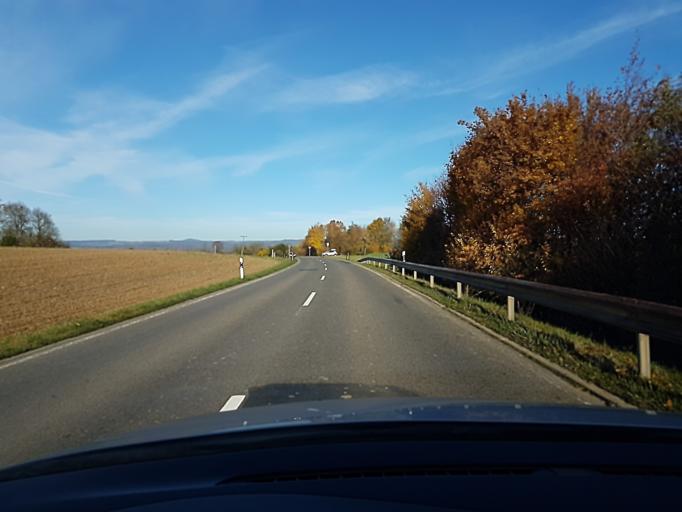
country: DE
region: Baden-Wuerttemberg
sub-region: Karlsruhe Region
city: Mosbach
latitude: 49.3691
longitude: 9.2009
